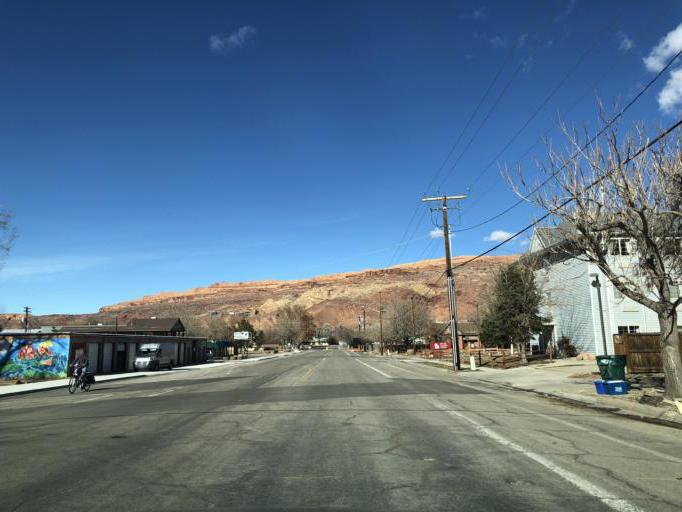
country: US
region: Utah
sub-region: Grand County
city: Moab
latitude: 38.5756
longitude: -109.5527
